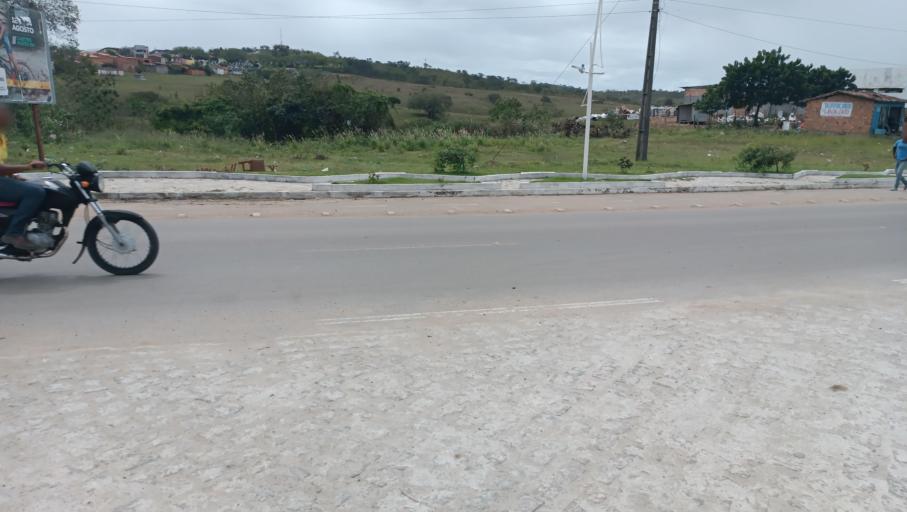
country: BR
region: Bahia
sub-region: Castro Alves
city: Castro Alves
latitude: -12.7639
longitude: -39.4219
